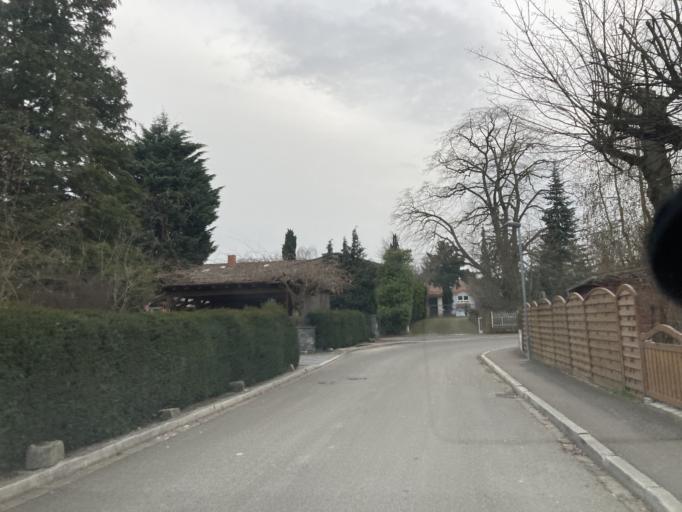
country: DE
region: Baden-Wuerttemberg
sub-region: Freiburg Region
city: Neuenburg am Rhein
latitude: 47.8126
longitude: 7.5701
